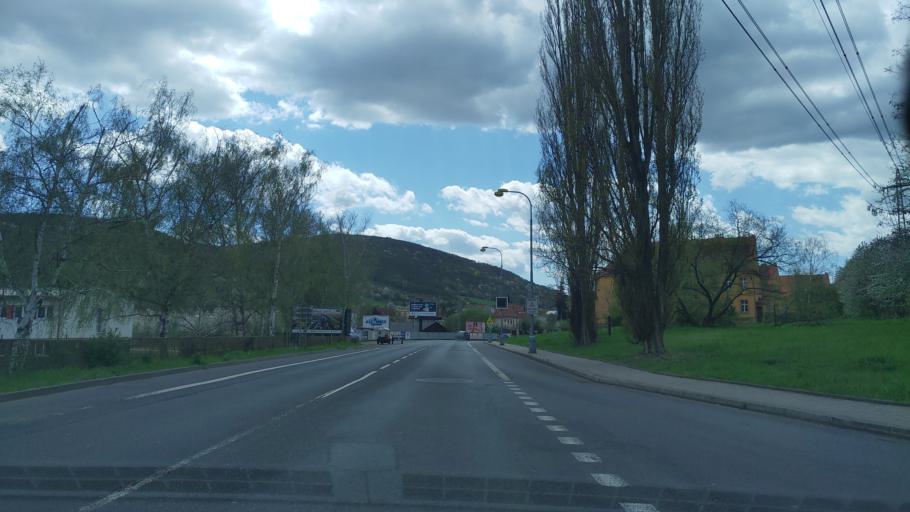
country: CZ
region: Ustecky
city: Trmice
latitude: 50.6471
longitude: 14.0045
